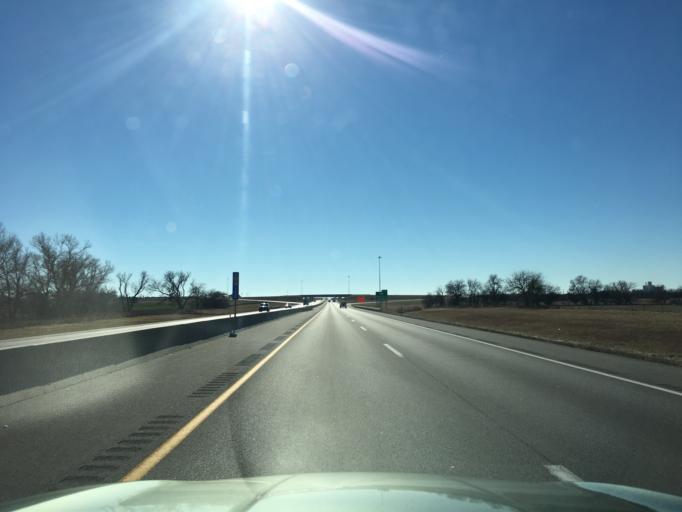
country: US
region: Kansas
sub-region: Sumner County
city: Wellington
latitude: 37.2856
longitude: -97.3403
